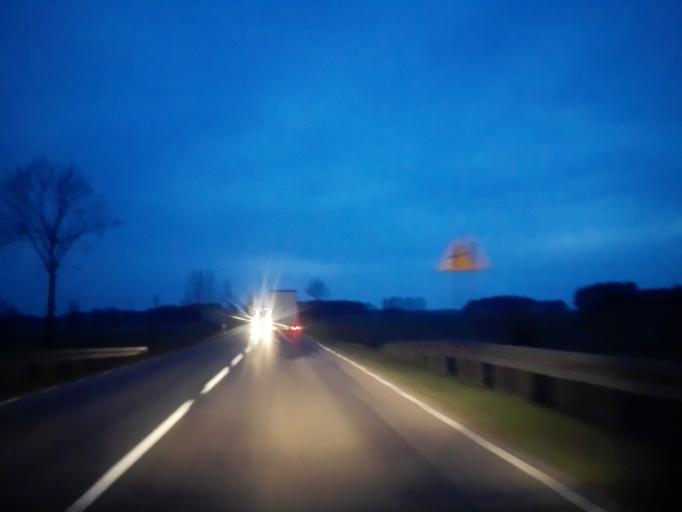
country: PL
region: Podlasie
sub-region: Powiat lomzynski
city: Sniadowo
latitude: 53.0707
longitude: 22.0122
